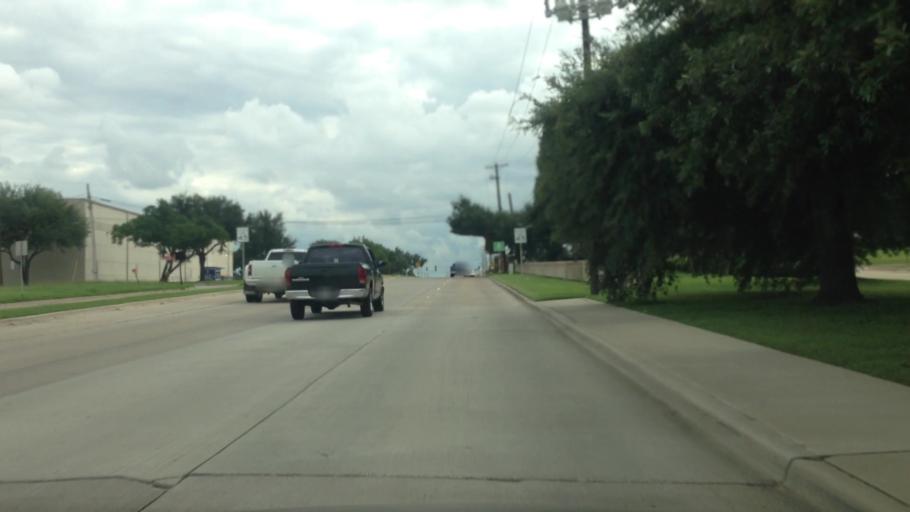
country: US
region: Texas
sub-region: Dallas County
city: Farmers Branch
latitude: 32.9216
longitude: -96.9253
